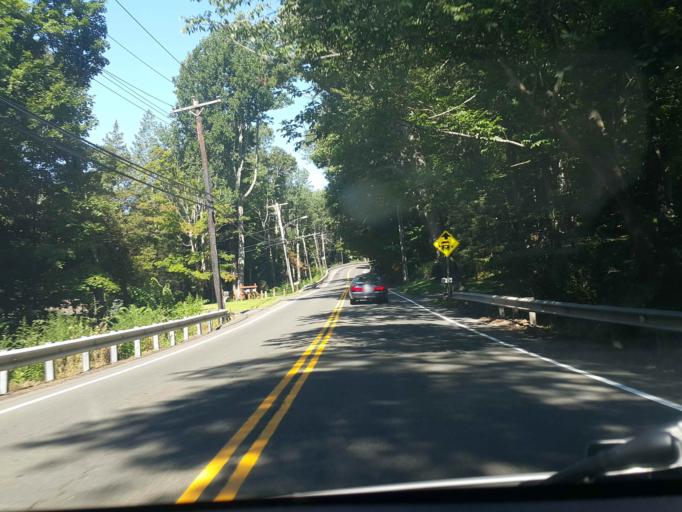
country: US
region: Connecticut
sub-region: New Haven County
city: North Branford
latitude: 41.3193
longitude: -72.7551
